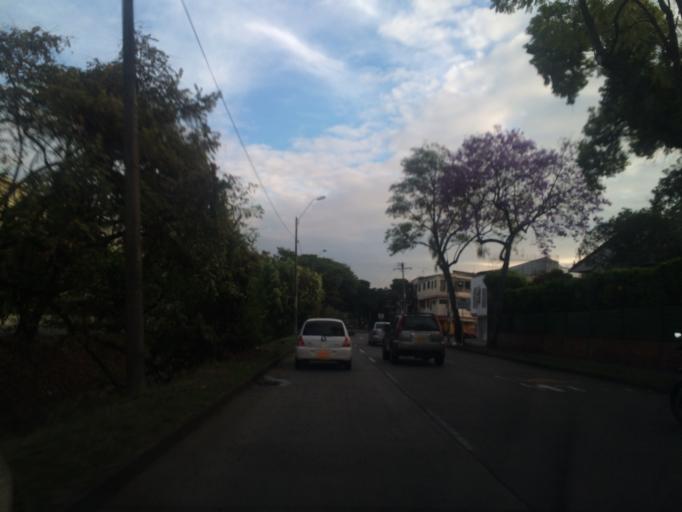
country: CO
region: Valle del Cauca
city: Cali
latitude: 3.4015
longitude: -76.5367
